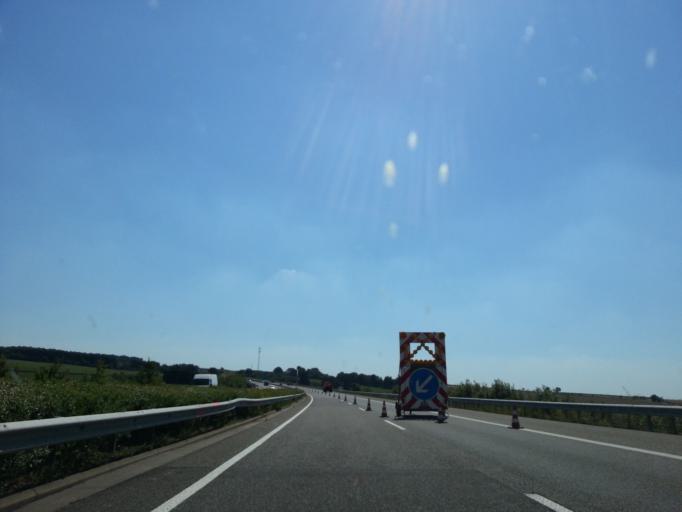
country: DE
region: Rheinland-Pfalz
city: Gransdorf
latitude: 50.0119
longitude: 6.6756
